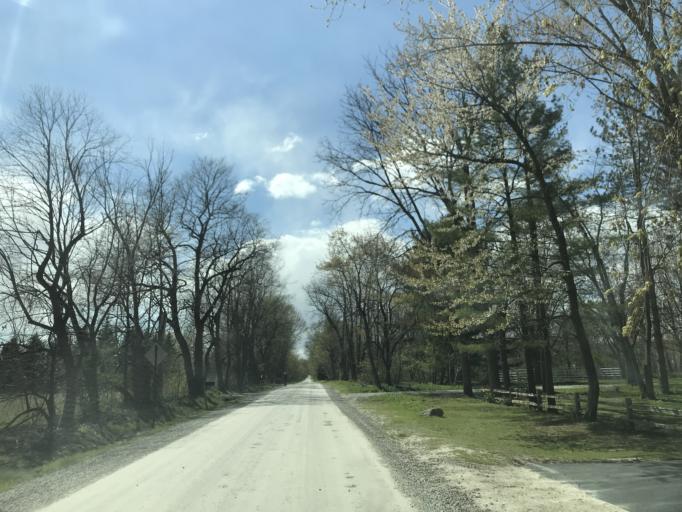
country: US
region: Michigan
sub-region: Oakland County
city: South Lyon
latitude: 42.4036
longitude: -83.6667
